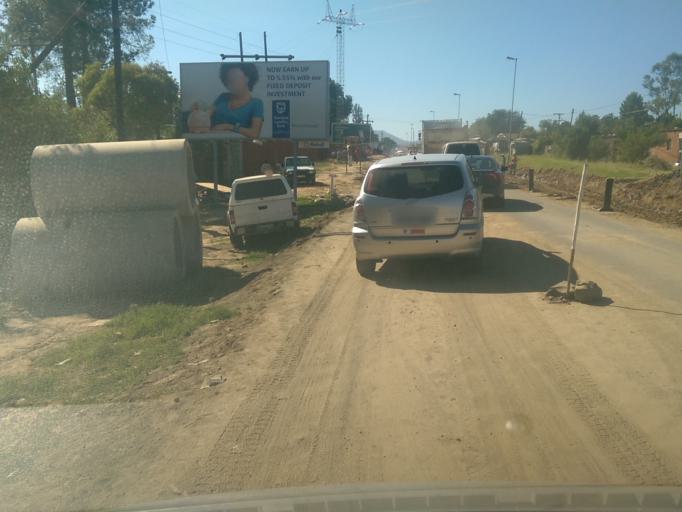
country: LS
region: Maseru
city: Nako
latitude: -29.4489
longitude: 27.7170
